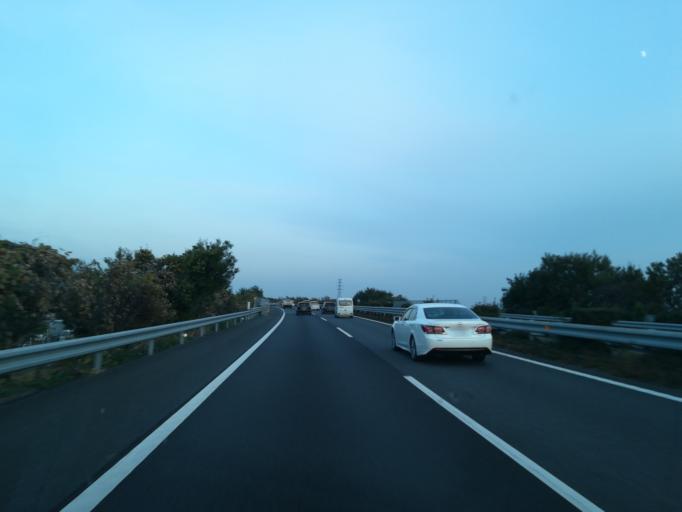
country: JP
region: Gunma
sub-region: Sawa-gun
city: Tamamura
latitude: 36.3370
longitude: 139.1255
